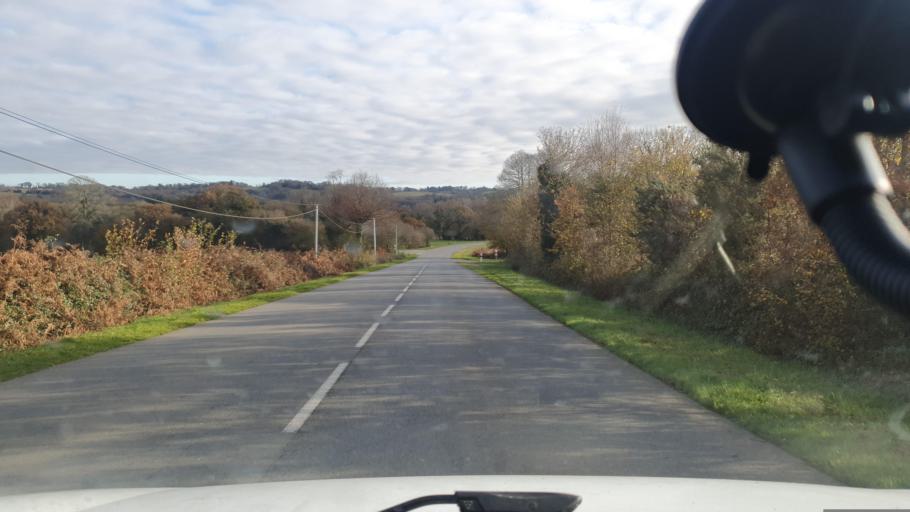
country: FR
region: Brittany
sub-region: Departement du Finistere
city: Edern
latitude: 48.0907
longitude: -3.9793
